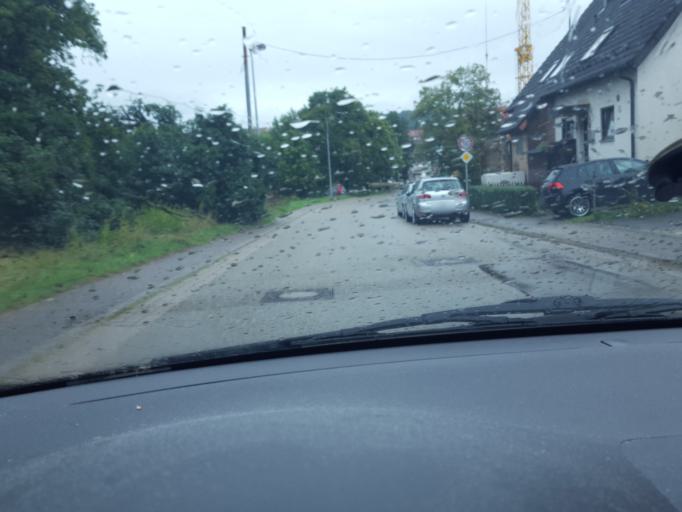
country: DE
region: Baden-Wuerttemberg
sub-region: Regierungsbezirk Stuttgart
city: Rudersberg
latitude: 48.8587
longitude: 9.5268
